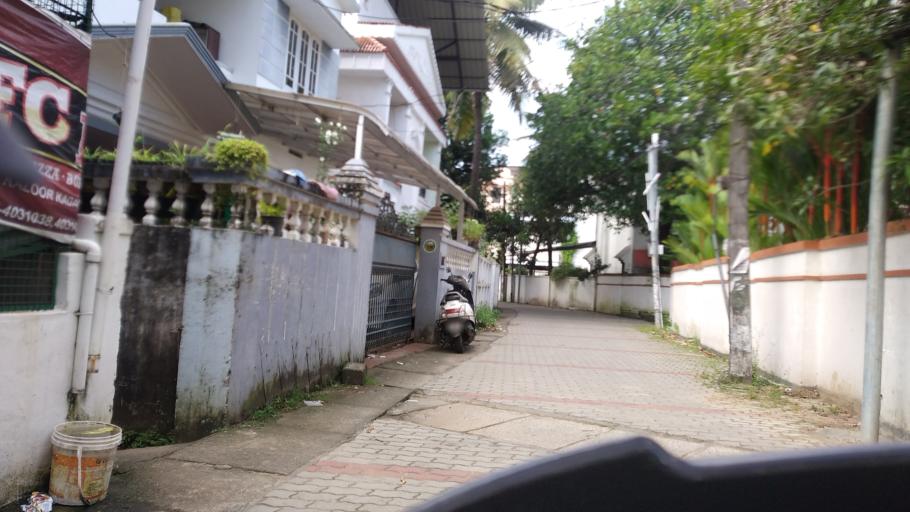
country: IN
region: Kerala
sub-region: Ernakulam
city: Cochin
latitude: 9.9887
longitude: 76.2995
